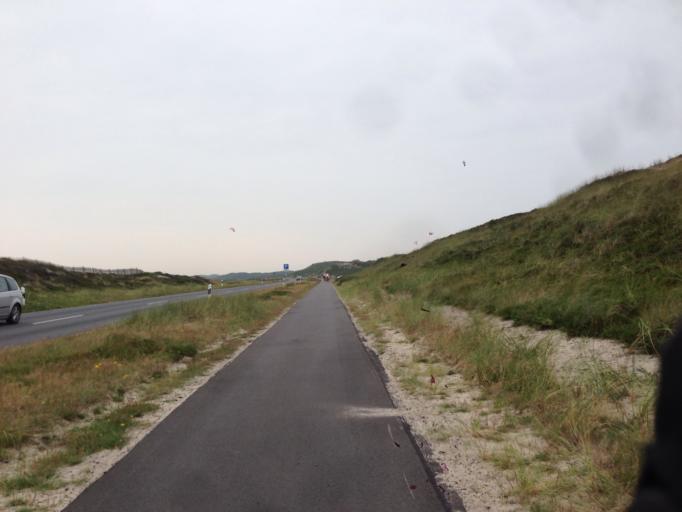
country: DE
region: Schleswig-Holstein
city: Westerland
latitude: 54.8127
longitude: 8.2897
